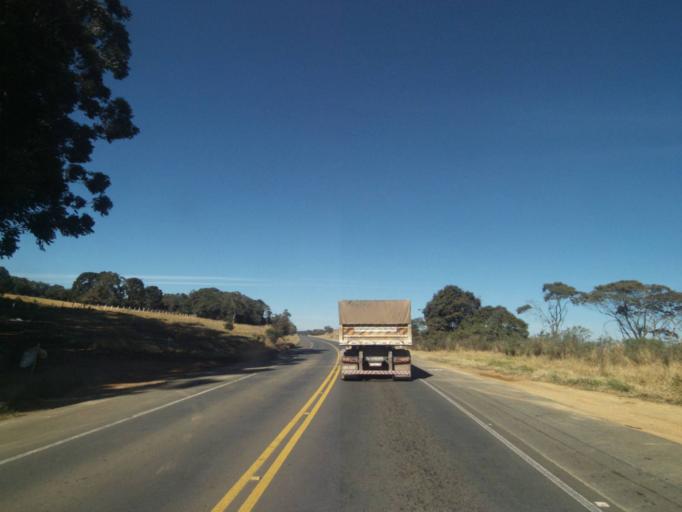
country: BR
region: Parana
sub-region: Tibagi
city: Tibagi
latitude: -24.7630
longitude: -50.4700
